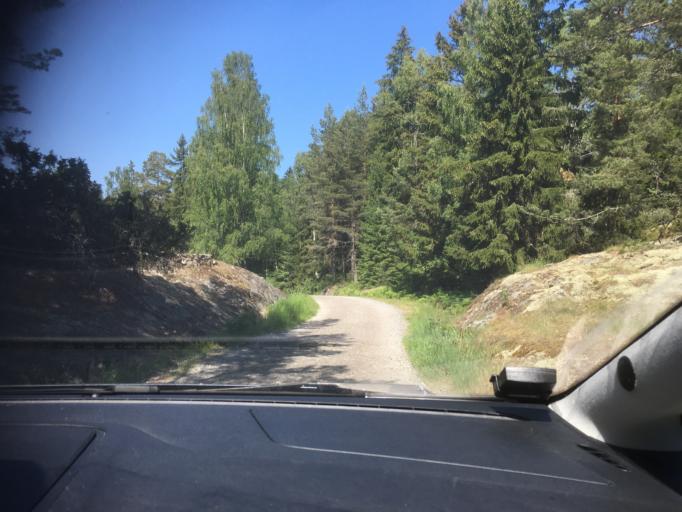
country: SE
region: Stockholm
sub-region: Haninge Kommun
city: Jordbro
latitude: 59.0132
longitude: 18.1651
